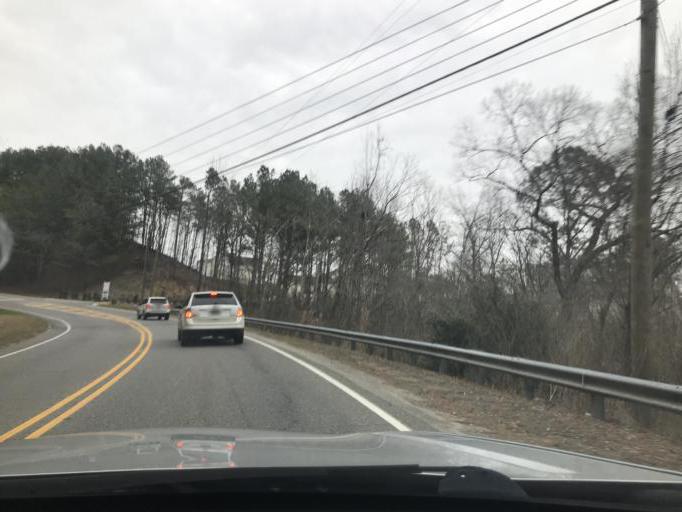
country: US
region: Alabama
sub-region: Jefferson County
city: Cahaba Heights
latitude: 33.4525
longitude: -86.7166
